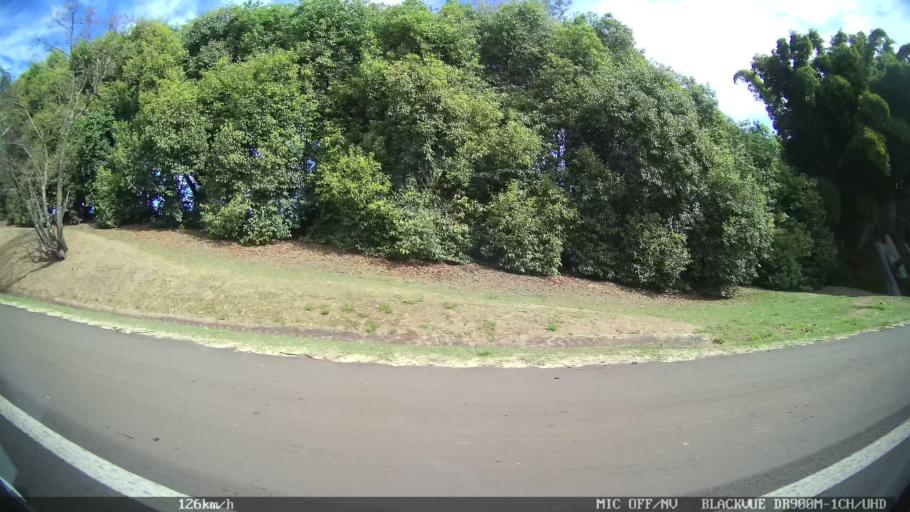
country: BR
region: Sao Paulo
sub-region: Matao
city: Matao
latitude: -21.6200
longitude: -48.4145
